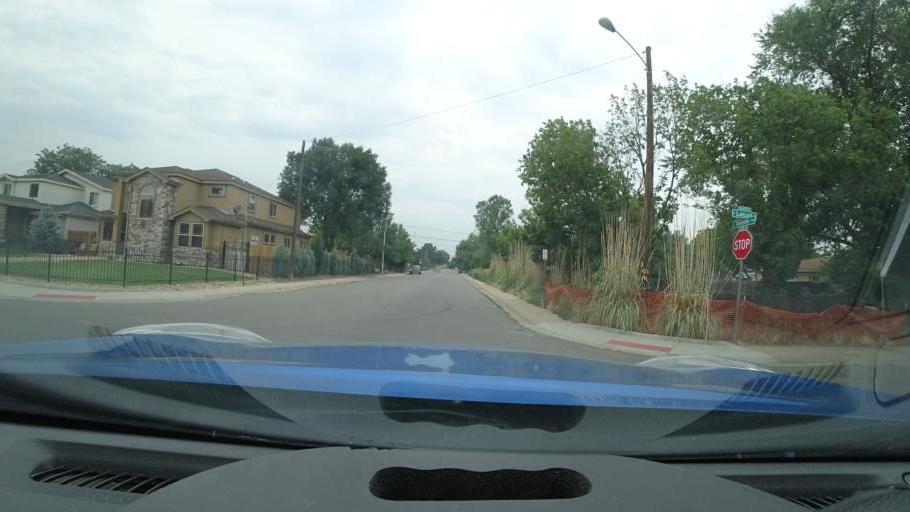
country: US
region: Colorado
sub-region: Arapahoe County
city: Glendale
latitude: 39.6985
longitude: -104.9141
